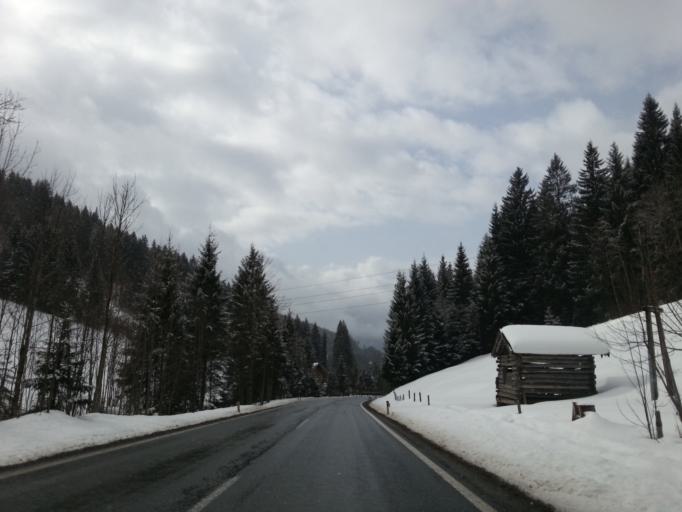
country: AT
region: Salzburg
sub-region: Politischer Bezirk Sankt Johann im Pongau
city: Eben im Pongau
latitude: 47.4466
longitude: 13.3641
